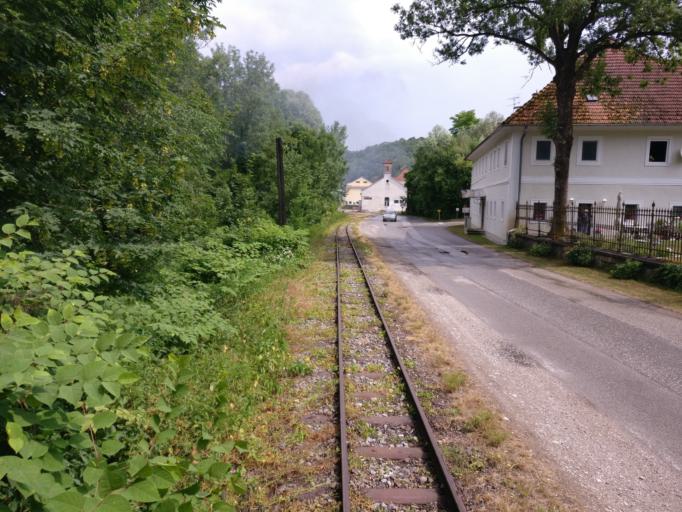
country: AT
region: Upper Austria
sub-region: Politischer Bezirk Steyr-Land
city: Sierning
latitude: 48.0310
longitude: 14.3372
